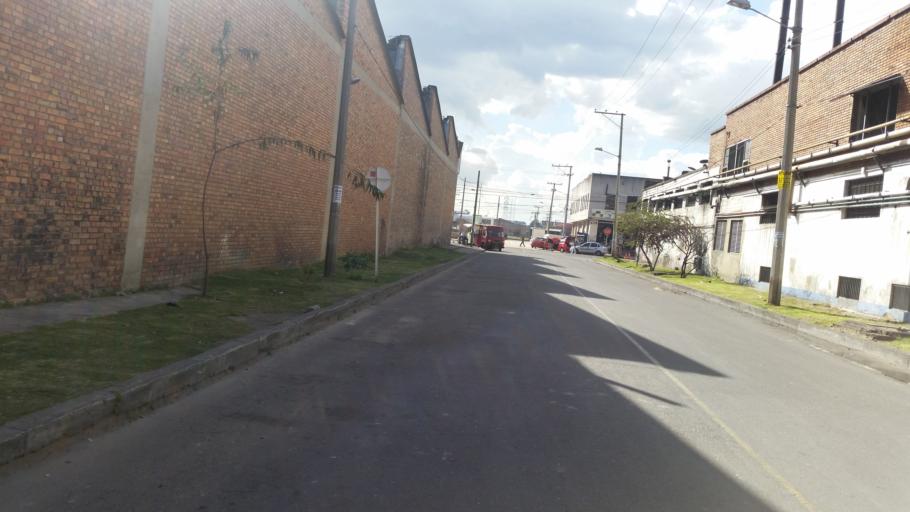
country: CO
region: Bogota D.C.
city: Bogota
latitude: 4.6187
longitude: -74.0995
